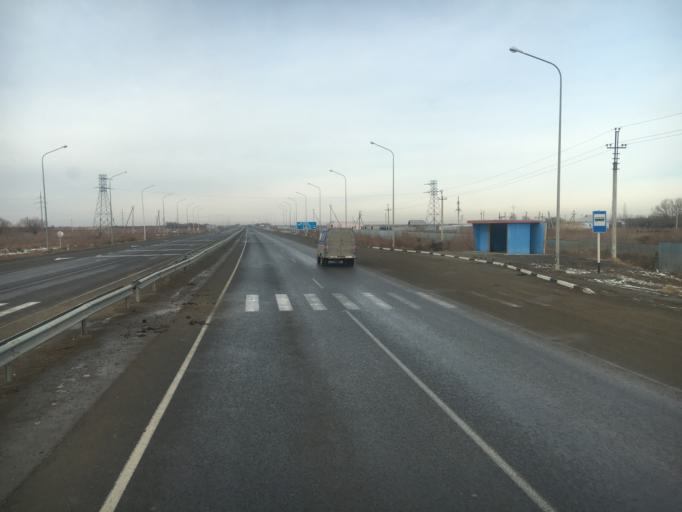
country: KZ
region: Qyzylorda
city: Shieli
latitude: 44.1384
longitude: 66.9674
